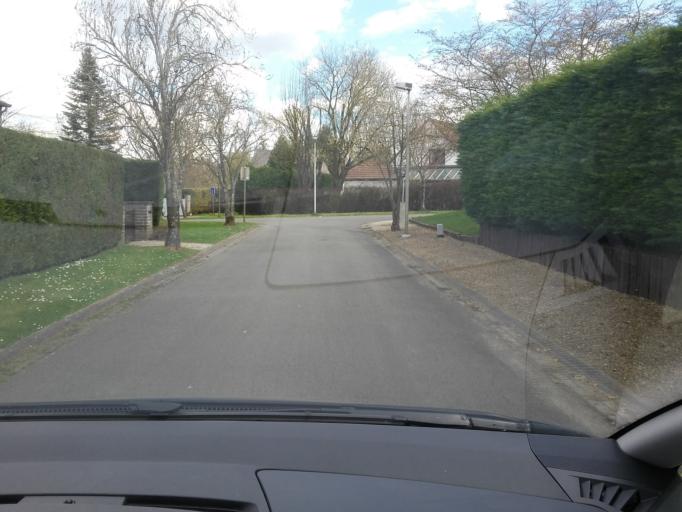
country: BE
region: Wallonia
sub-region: Province du Brabant Wallon
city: Waterloo
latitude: 50.7051
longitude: 4.4238
